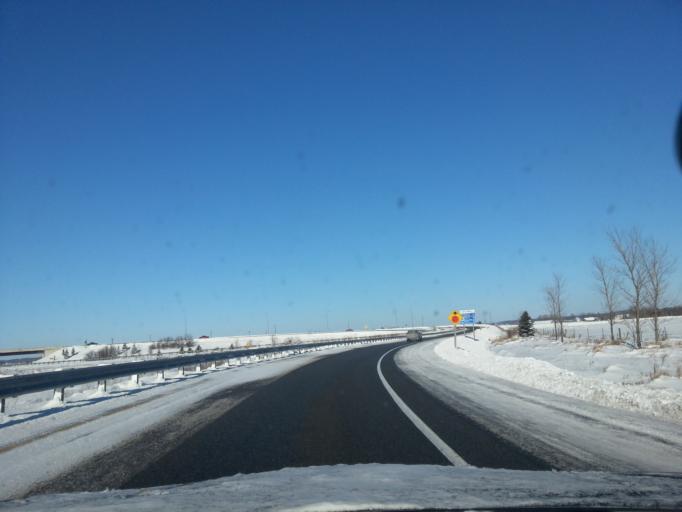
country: CA
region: Ontario
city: Arnprior
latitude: 45.3613
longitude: -76.2314
